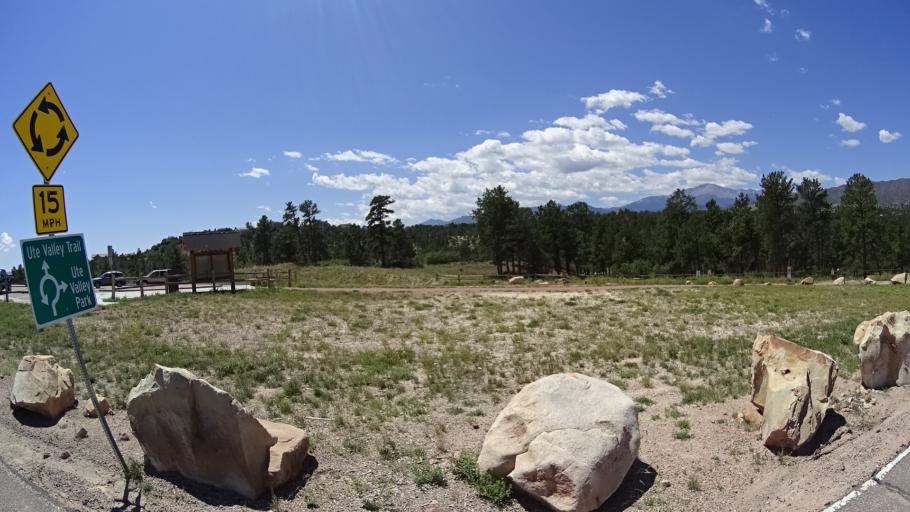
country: US
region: Colorado
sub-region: El Paso County
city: Colorado Springs
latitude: 38.9152
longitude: -104.8368
